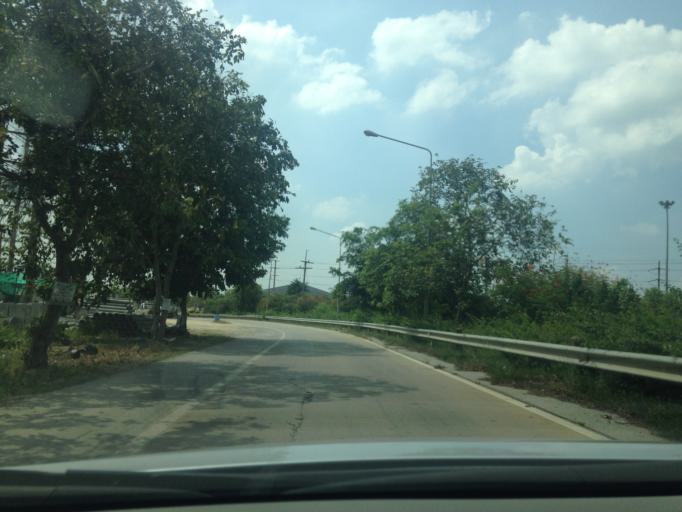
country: TH
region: Pathum Thani
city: Sam Khok
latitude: 14.0907
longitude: 100.5180
